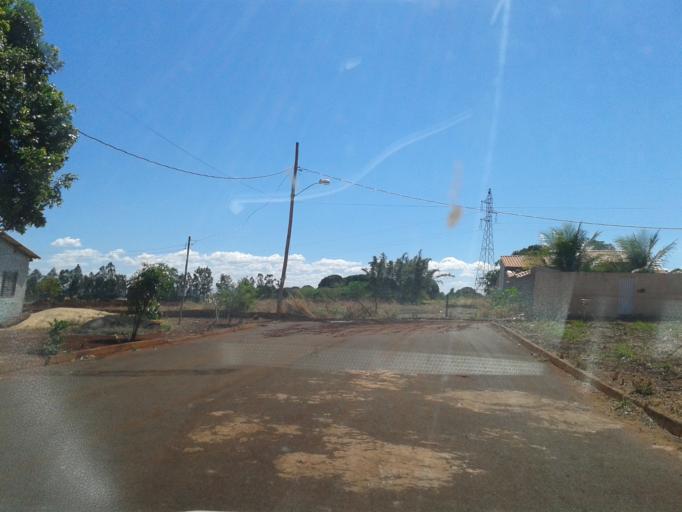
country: BR
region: Minas Gerais
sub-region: Centralina
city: Centralina
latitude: -18.5935
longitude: -49.2018
